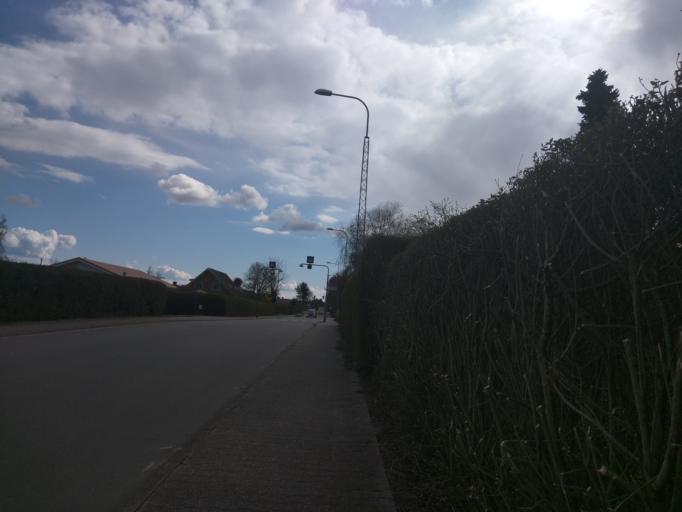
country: DK
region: South Denmark
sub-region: Fredericia Kommune
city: Snoghoj
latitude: 55.5434
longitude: 9.7120
